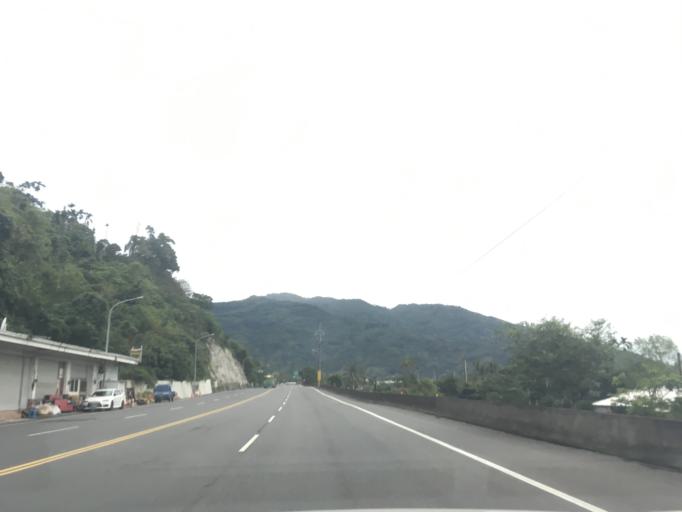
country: TW
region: Taiwan
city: Taitung City
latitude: 22.7527
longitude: 121.0539
